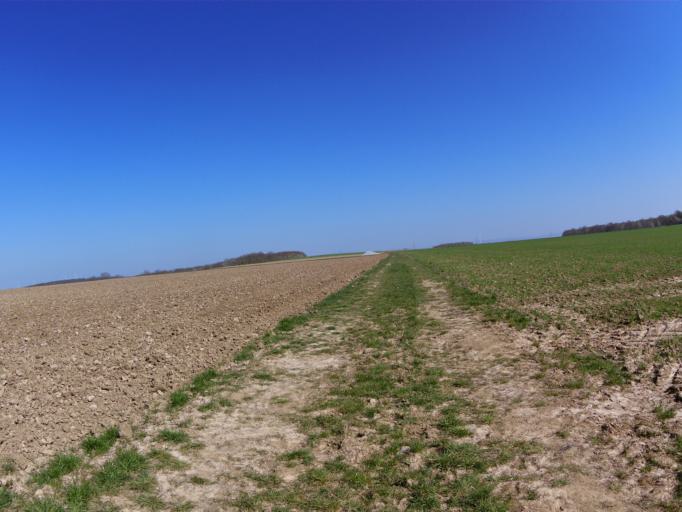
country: DE
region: Bavaria
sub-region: Regierungsbezirk Unterfranken
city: Kurnach
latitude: 49.8376
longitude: 10.0526
